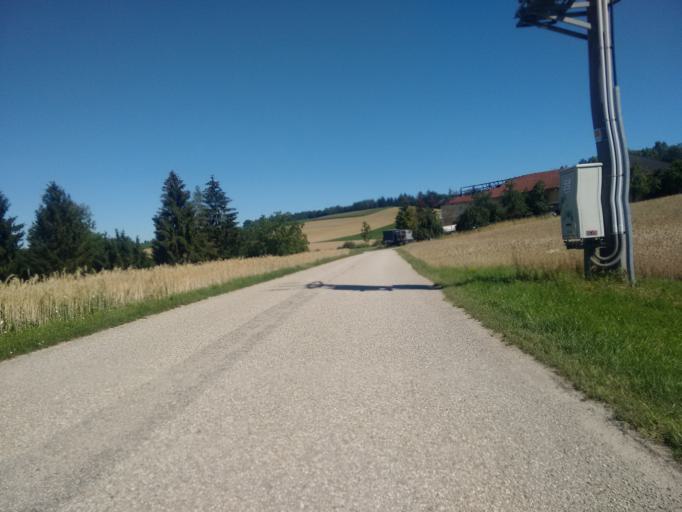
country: AT
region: Upper Austria
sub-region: Wels-Land
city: Buchkirchen
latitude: 48.2242
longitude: 13.9829
